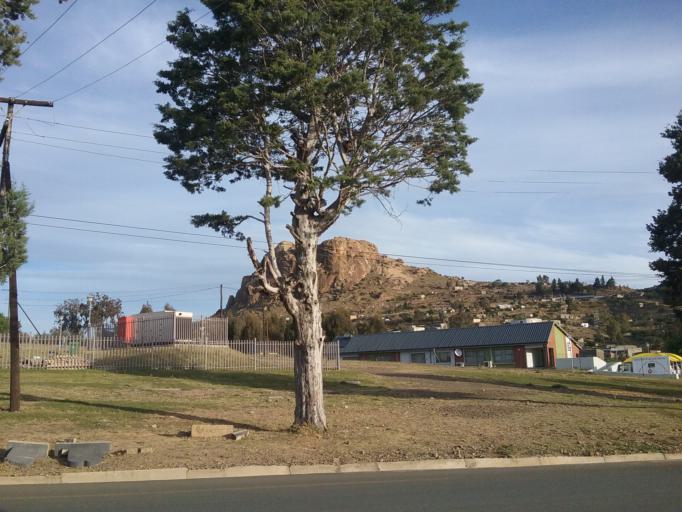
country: LS
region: Maseru
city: Maseru
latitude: -29.3463
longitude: 27.5256
